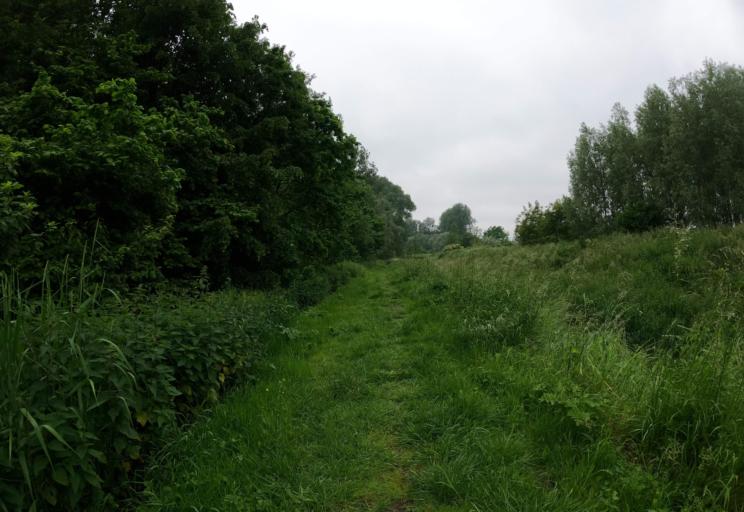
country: BE
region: Flanders
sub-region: Provincie Antwerpen
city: Puurs
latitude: 51.0700
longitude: 4.2655
